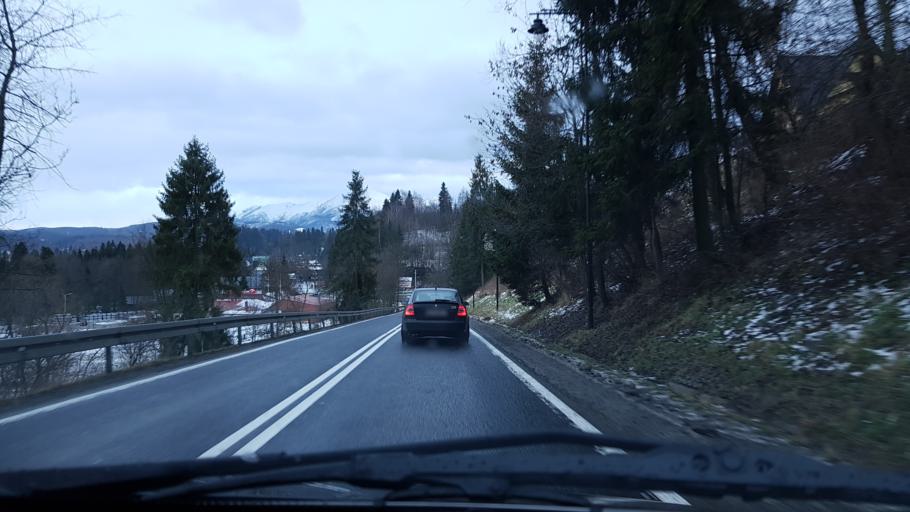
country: PL
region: Lesser Poland Voivodeship
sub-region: Powiat tatrzanski
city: Czarna Gora
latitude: 49.3672
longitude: 20.1145
